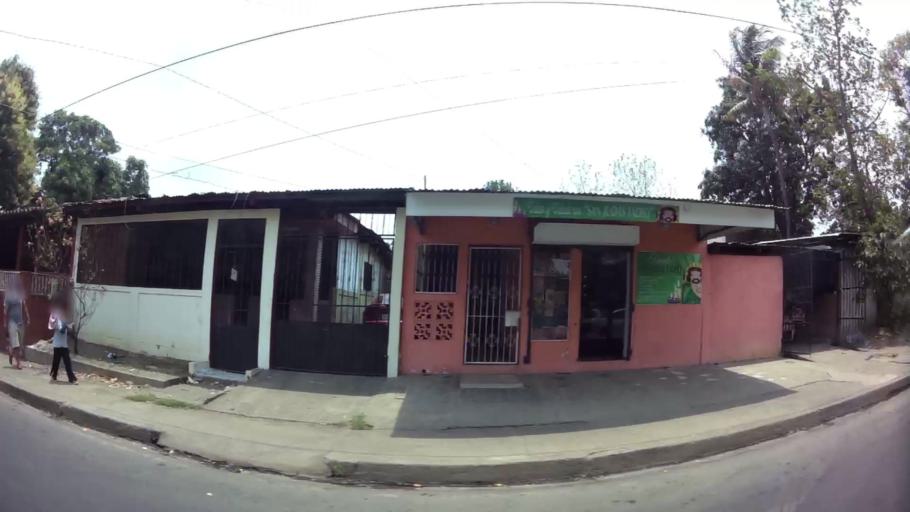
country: NI
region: Managua
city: Managua
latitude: 12.1121
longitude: -86.2980
